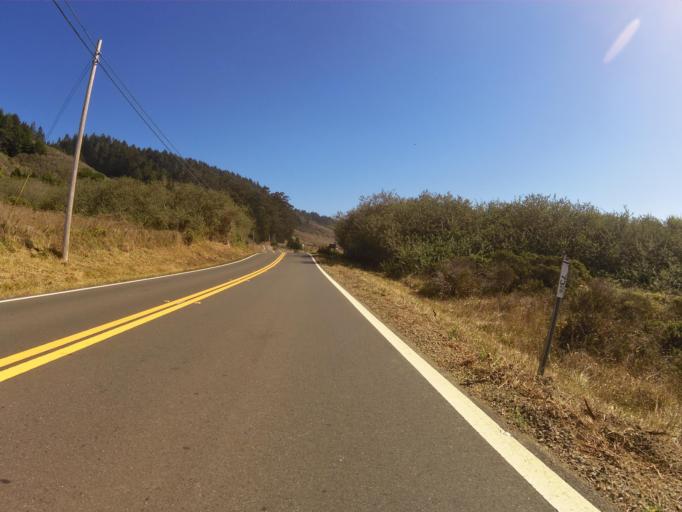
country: US
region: California
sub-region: Mendocino County
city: Fort Bragg
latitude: 39.5888
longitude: -123.7766
